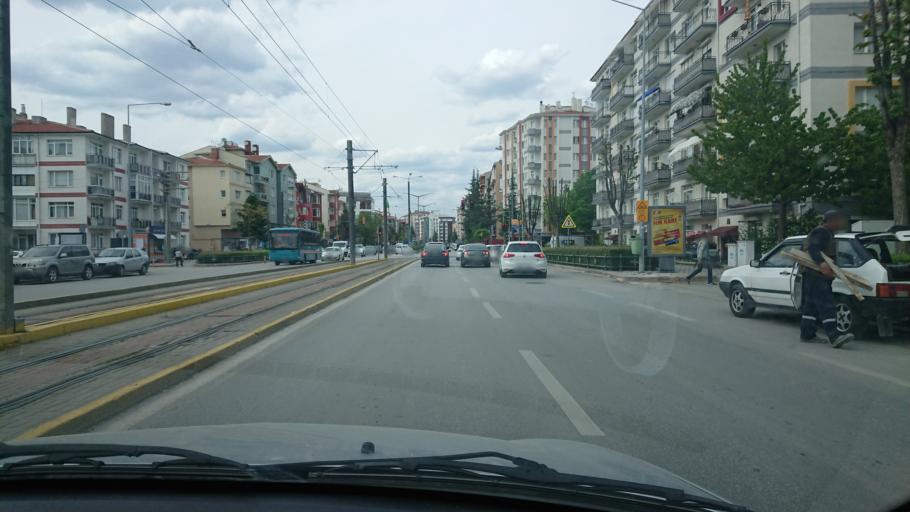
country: TR
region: Eskisehir
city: Eskisehir
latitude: 39.7667
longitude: 30.5008
